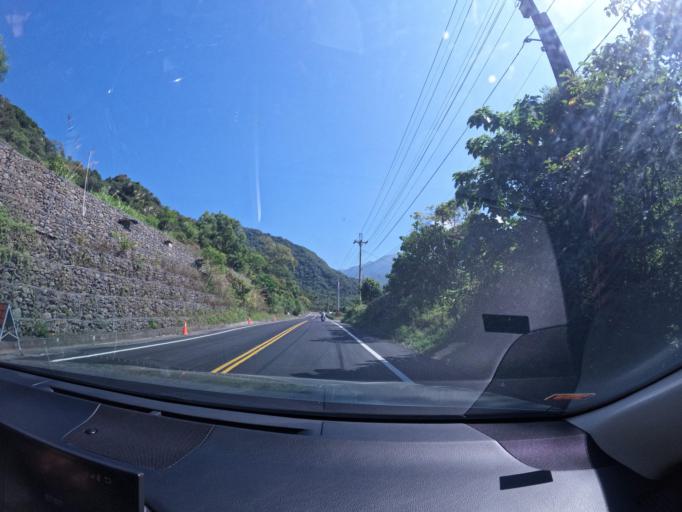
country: TW
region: Taiwan
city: Yujing
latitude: 23.1380
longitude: 120.7385
